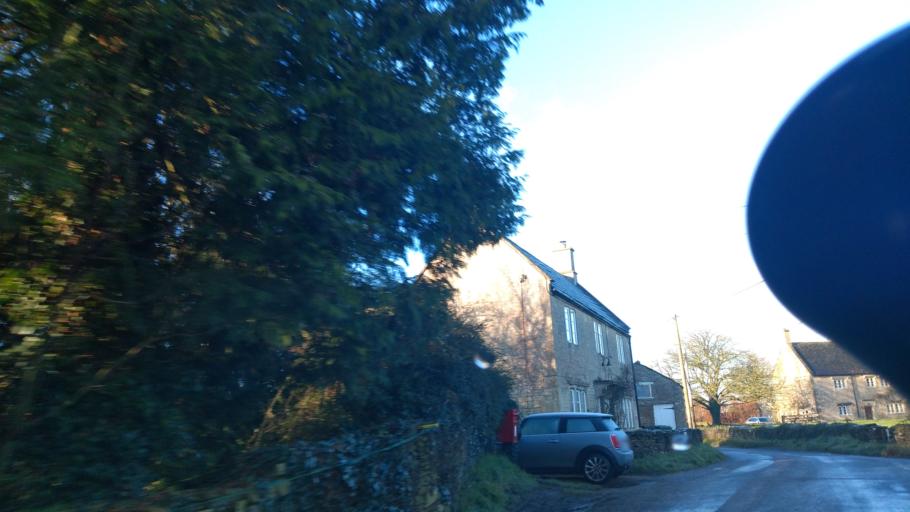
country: GB
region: England
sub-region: Wiltshire
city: Corsham
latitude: 51.4134
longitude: -2.1571
